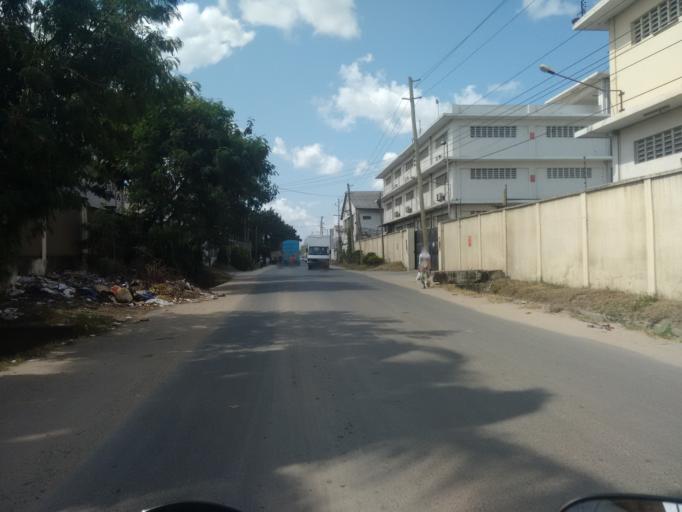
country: TZ
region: Dar es Salaam
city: Dar es Salaam
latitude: -6.8404
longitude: 39.2645
